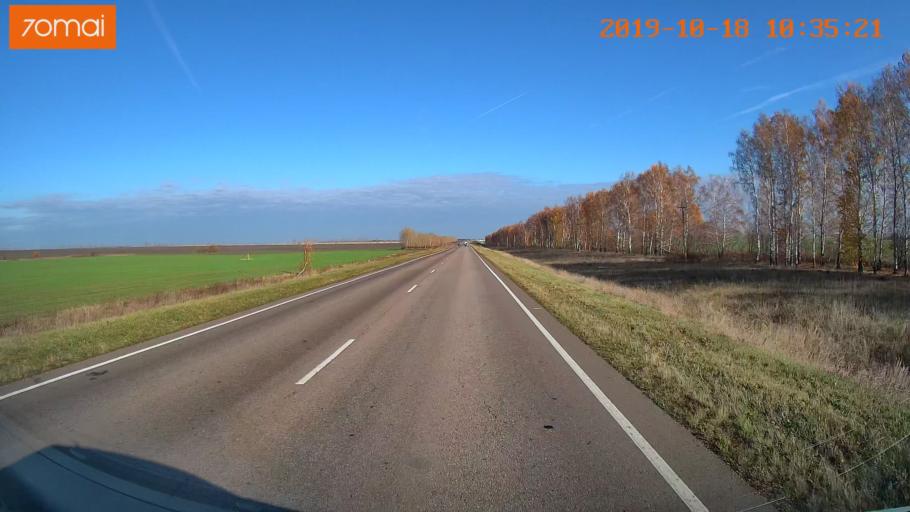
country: RU
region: Tula
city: Kurkino
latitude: 53.5317
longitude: 38.6193
